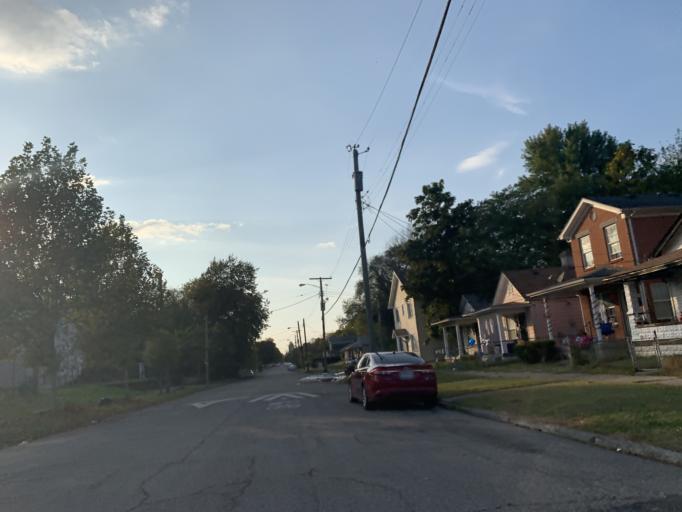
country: US
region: Kentucky
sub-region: Jefferson County
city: Louisville
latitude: 38.2347
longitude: -85.7806
